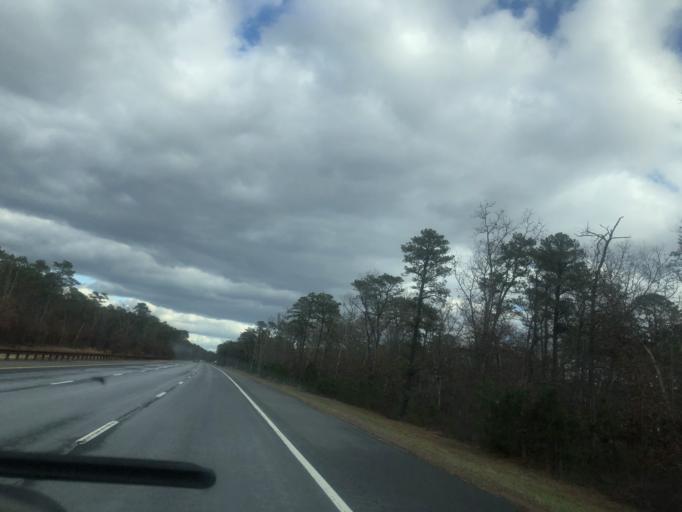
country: US
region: New Jersey
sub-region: Ocean County
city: Tuckerton
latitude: 39.6282
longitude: -74.3881
